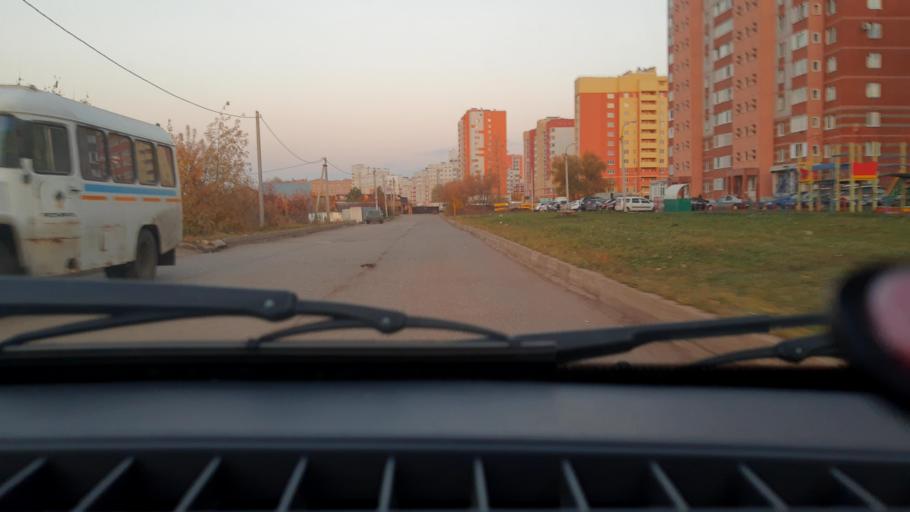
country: RU
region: Bashkortostan
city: Mikhaylovka
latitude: 54.7137
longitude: 55.8275
